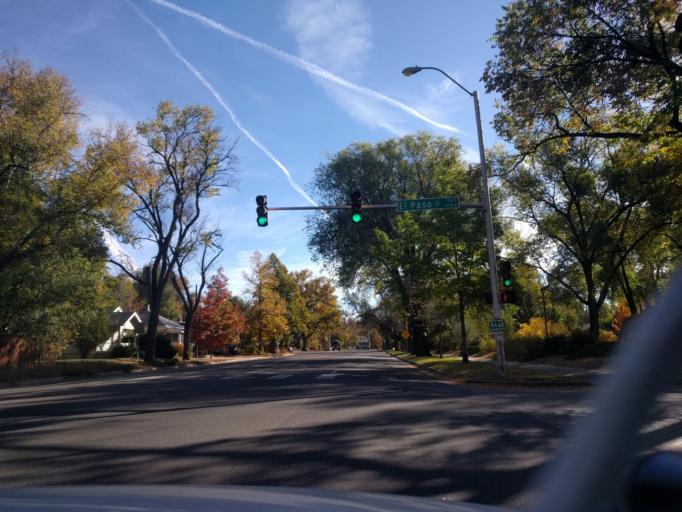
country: US
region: Colorado
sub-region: El Paso County
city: Colorado Springs
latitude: 38.8503
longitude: -104.8127
